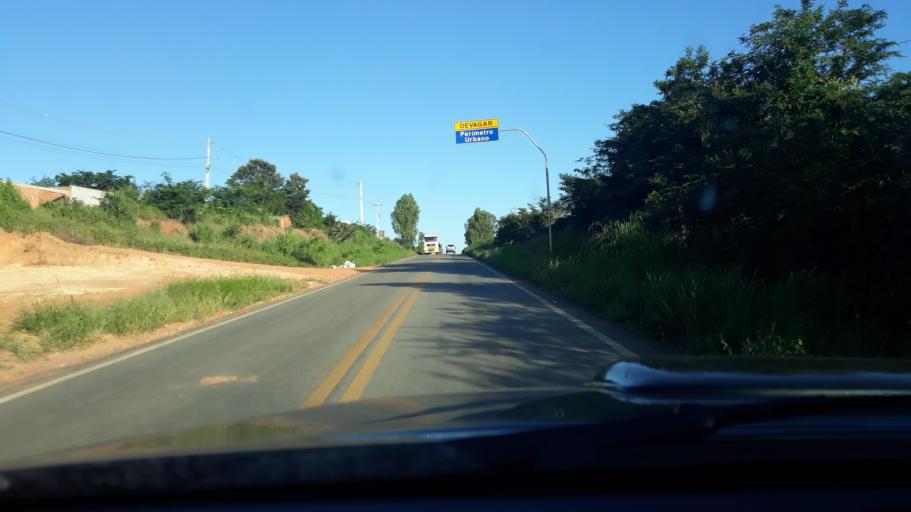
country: BR
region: Bahia
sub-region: Riacho De Santana
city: Riacho de Santana
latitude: -13.7657
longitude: -42.7252
